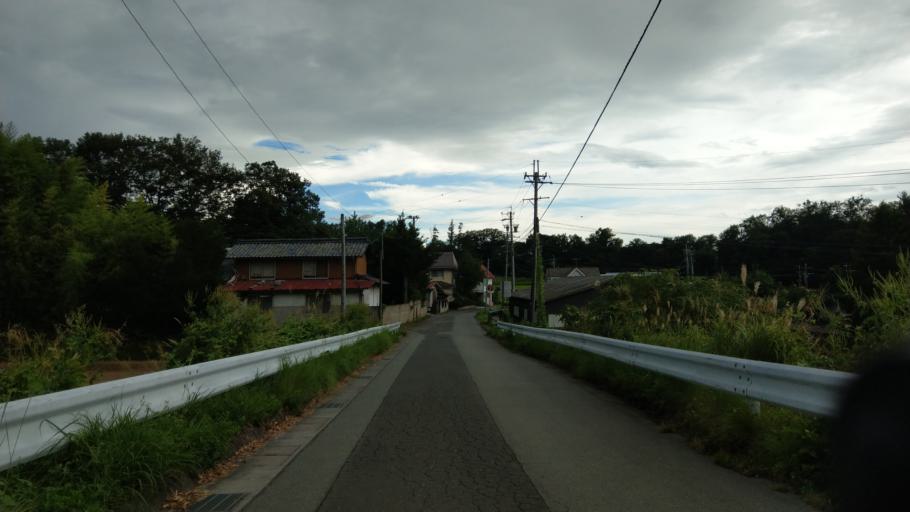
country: JP
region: Nagano
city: Komoro
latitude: 36.3119
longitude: 138.4698
